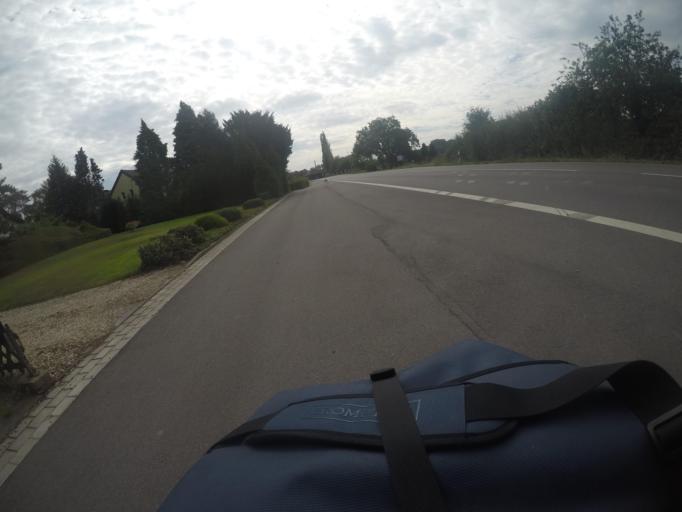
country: DE
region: North Rhine-Westphalia
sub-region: Regierungsbezirk Dusseldorf
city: Emmerich
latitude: 51.8445
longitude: 6.2121
